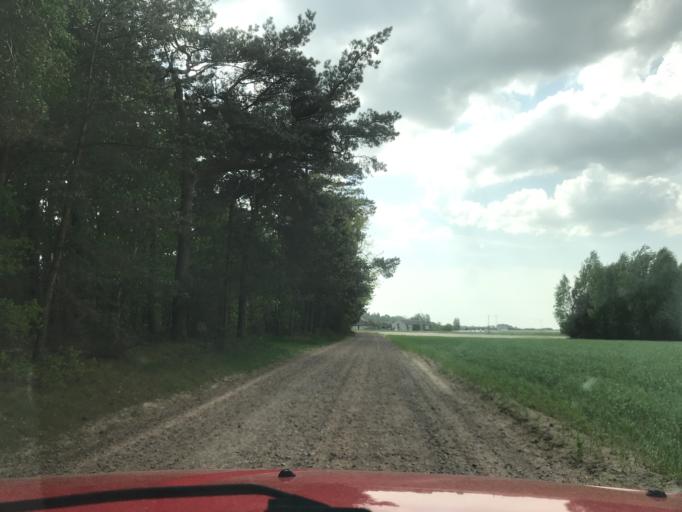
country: PL
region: Greater Poland Voivodeship
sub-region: Powiat turecki
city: Tuliszkow
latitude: 51.9577
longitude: 18.2610
